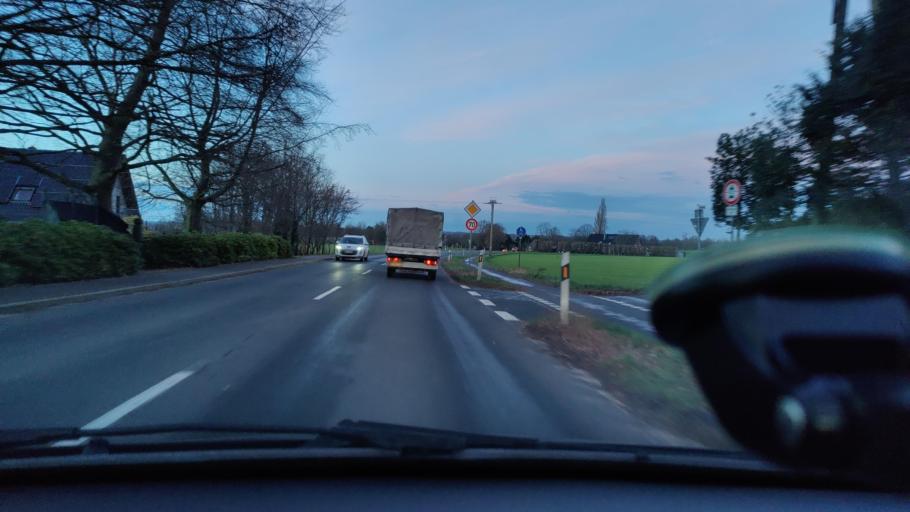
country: DE
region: North Rhine-Westphalia
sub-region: Regierungsbezirk Dusseldorf
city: Xanten
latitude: 51.6494
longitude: 6.4567
